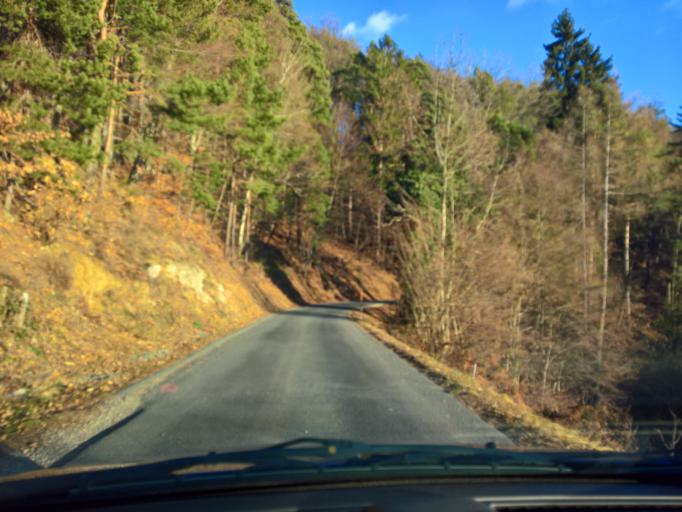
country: AT
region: Styria
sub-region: Politischer Bezirk Leibnitz
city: Leutschach
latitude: 46.6927
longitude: 15.4433
